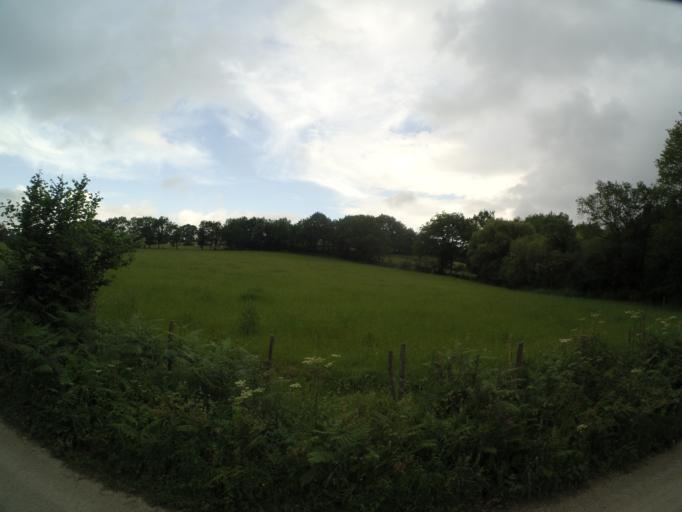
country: FR
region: Pays de la Loire
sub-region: Departement de la Vendee
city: Nesmy
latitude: 46.6078
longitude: -1.3833
